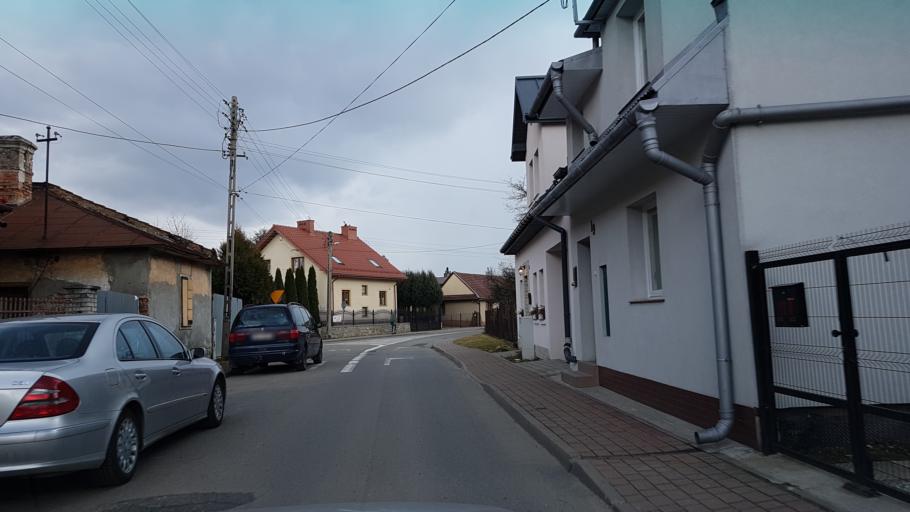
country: PL
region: Lesser Poland Voivodeship
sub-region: Powiat nowosadecki
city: Stary Sacz
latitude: 49.5600
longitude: 20.6344
